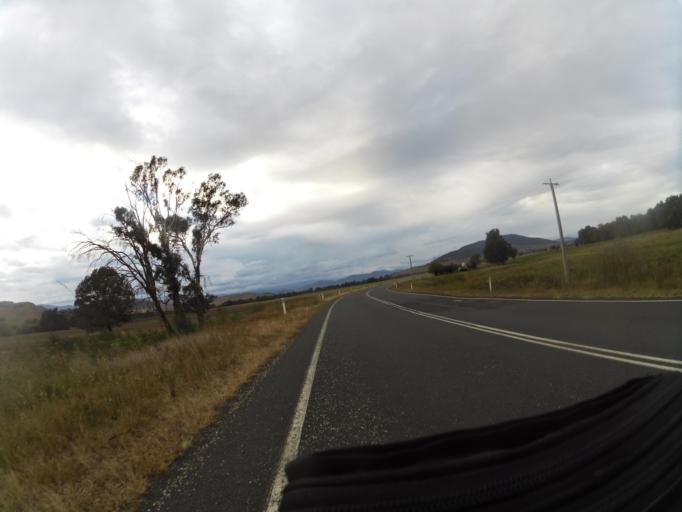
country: AU
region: New South Wales
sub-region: Snowy River
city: Jindabyne
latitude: -36.0922
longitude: 147.9815
